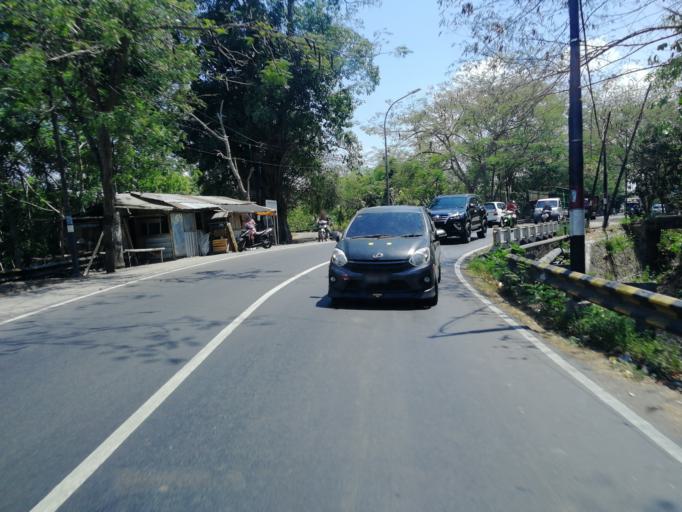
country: ID
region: West Nusa Tenggara
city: Jelateng Timur
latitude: -8.6933
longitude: 116.1090
